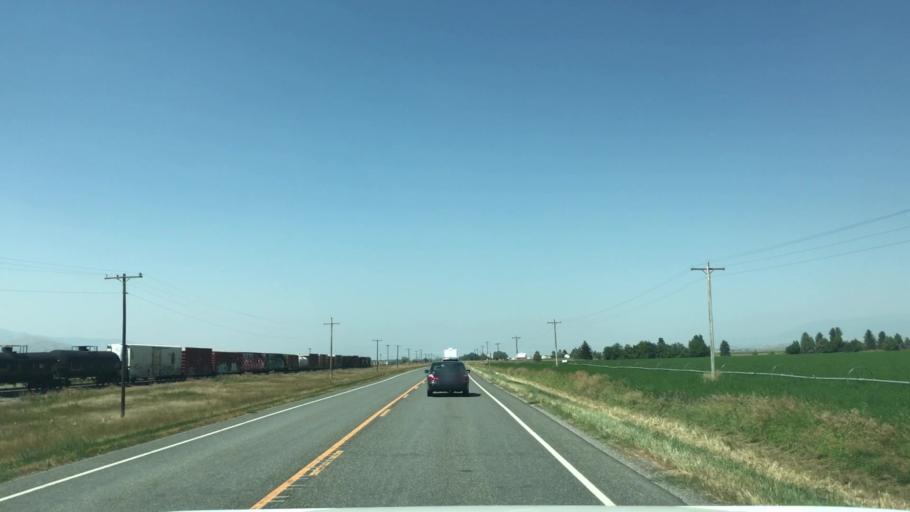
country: US
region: Montana
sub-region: Broadwater County
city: Townsend
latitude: 46.1916
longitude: -111.4491
